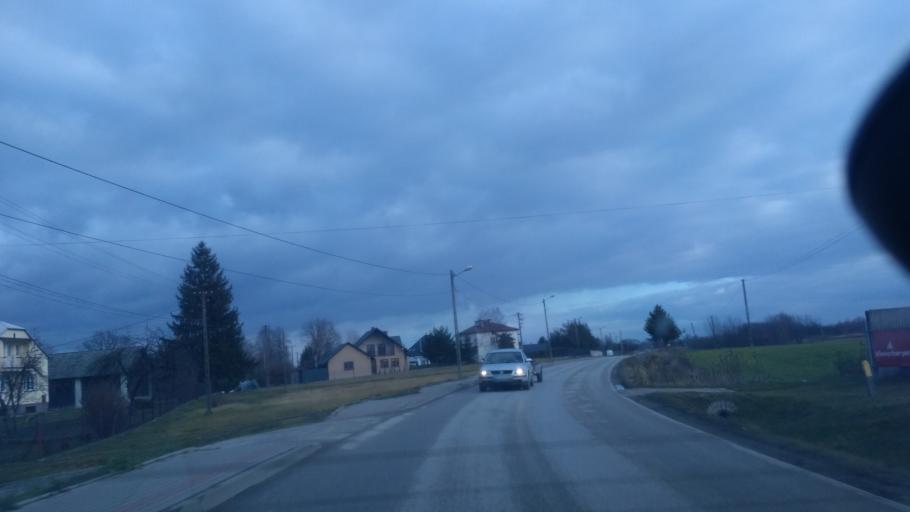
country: PL
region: Subcarpathian Voivodeship
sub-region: Powiat lancucki
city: Czarna
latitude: 50.1144
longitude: 22.2082
